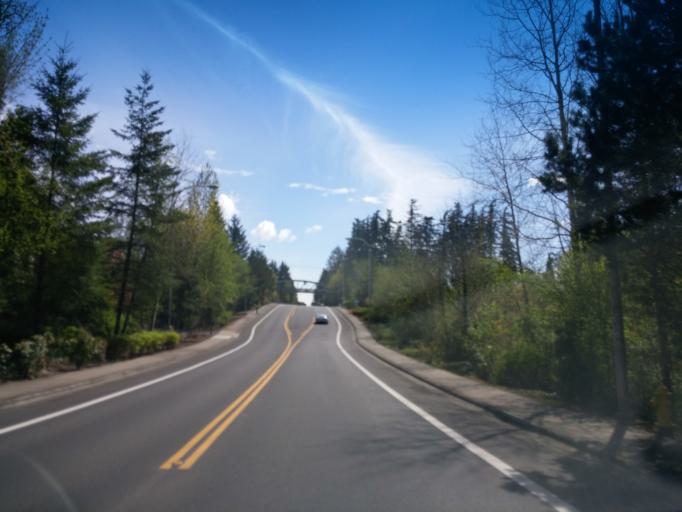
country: US
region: Oregon
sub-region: Washington County
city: Cedar Mill
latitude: 45.5282
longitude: -122.7929
